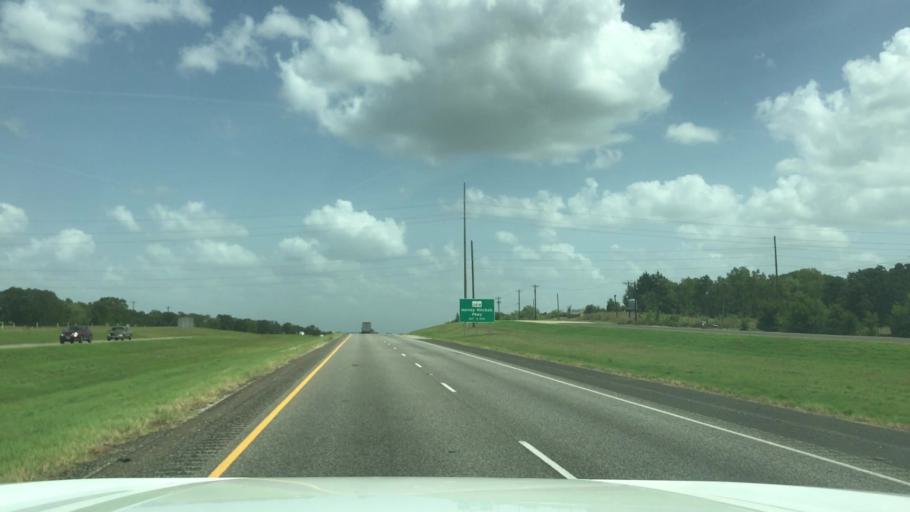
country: US
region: Texas
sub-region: Brazos County
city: Bryan
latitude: 30.7410
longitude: -96.4452
